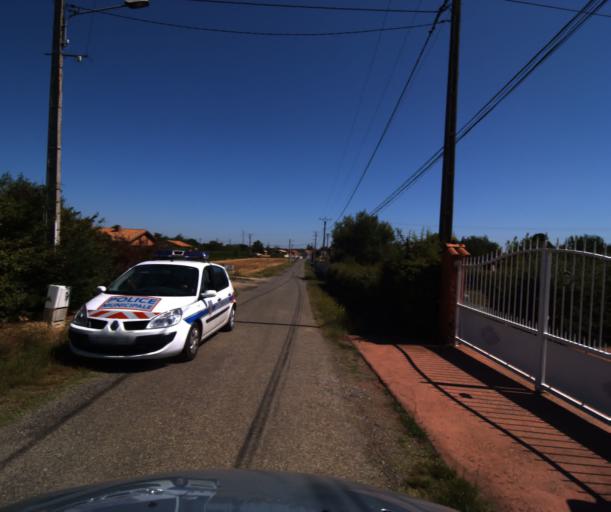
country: FR
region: Midi-Pyrenees
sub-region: Departement de la Haute-Garonne
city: Muret
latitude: 43.4573
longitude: 1.3608
